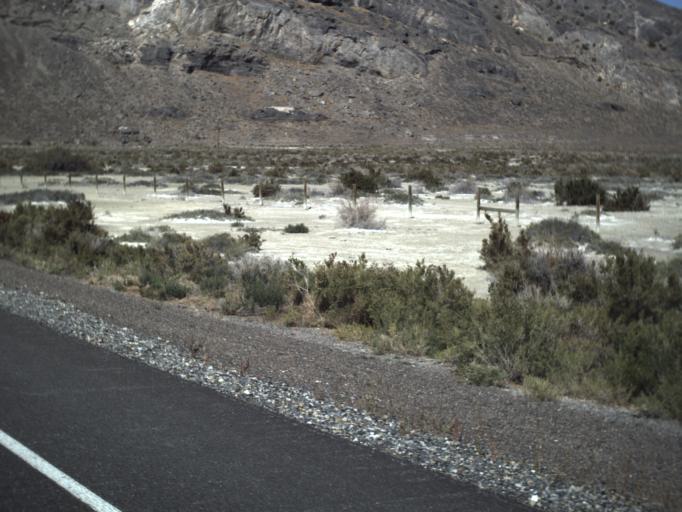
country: US
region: Utah
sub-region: Tooele County
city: Wendover
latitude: 40.7489
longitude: -114.0102
